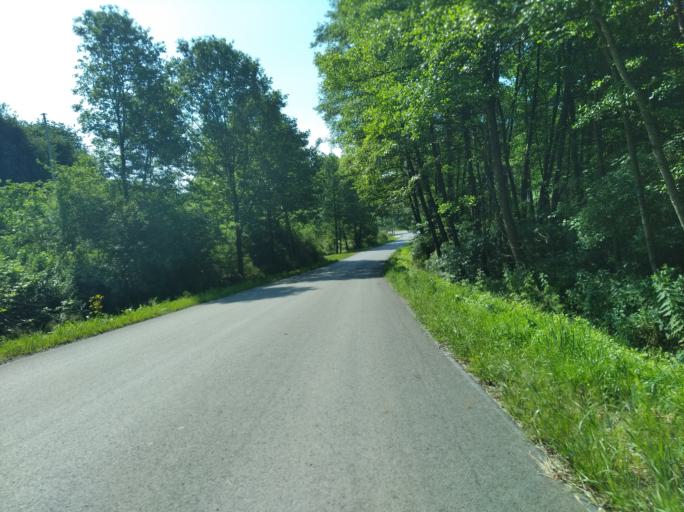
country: PL
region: Subcarpathian Voivodeship
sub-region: Powiat brzozowski
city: Wesola
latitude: 49.8295
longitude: 22.1496
